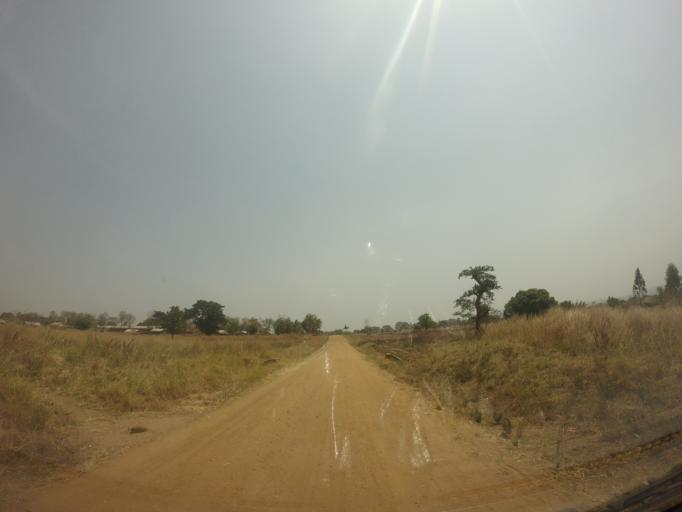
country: UG
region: Northern Region
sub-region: Arua District
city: Arua
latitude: 2.9149
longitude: 31.0204
